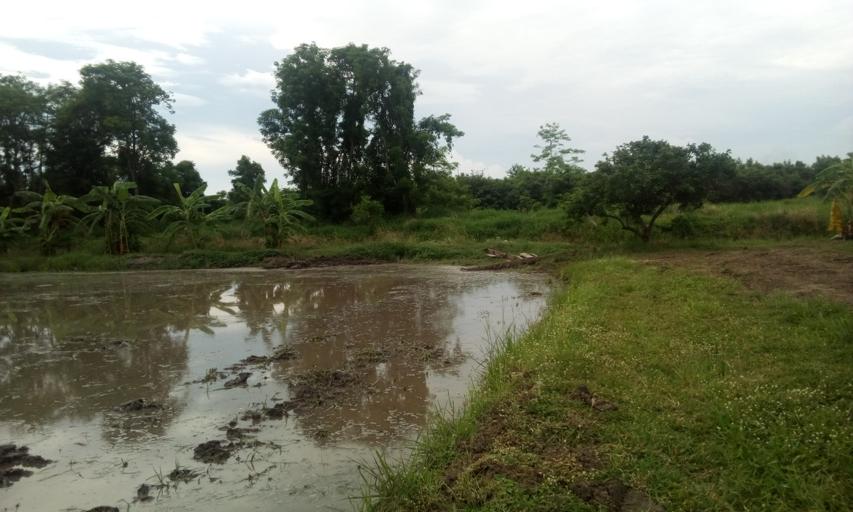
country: TH
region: Pathum Thani
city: Ban Lam Luk Ka
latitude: 13.9907
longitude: 100.8366
